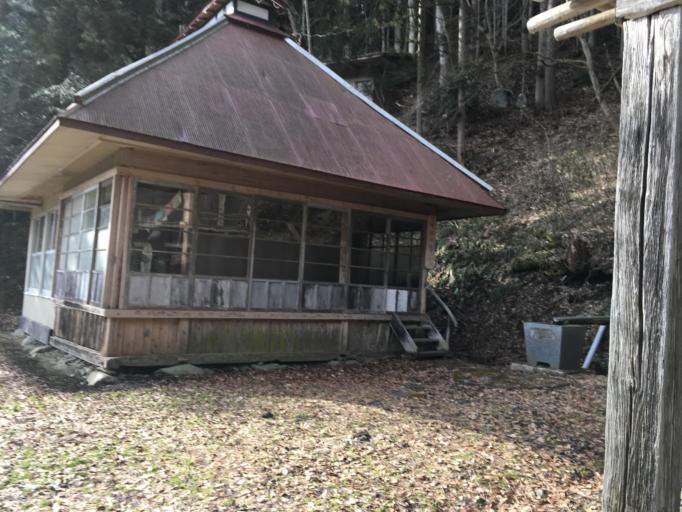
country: JP
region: Iwate
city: Tono
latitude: 39.2378
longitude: 141.3382
